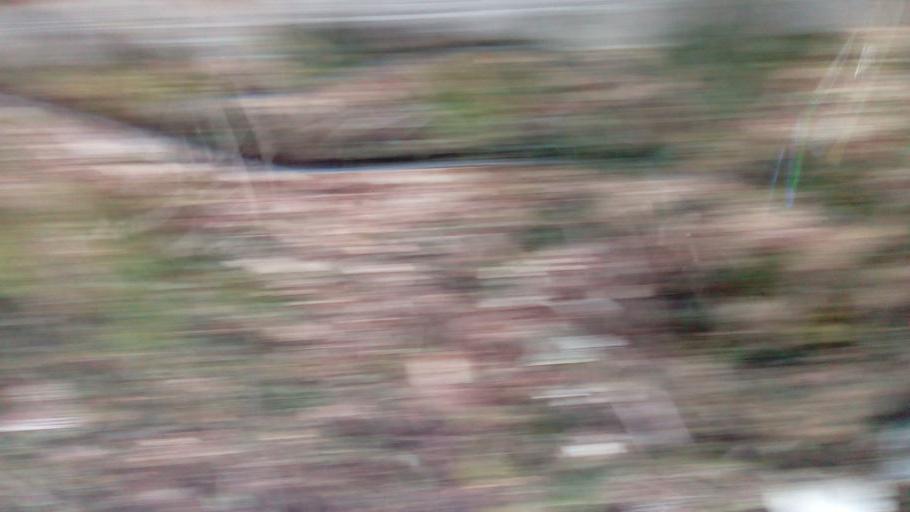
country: TW
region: Taiwan
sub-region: Hualien
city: Hualian
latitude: 24.3540
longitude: 121.3251
